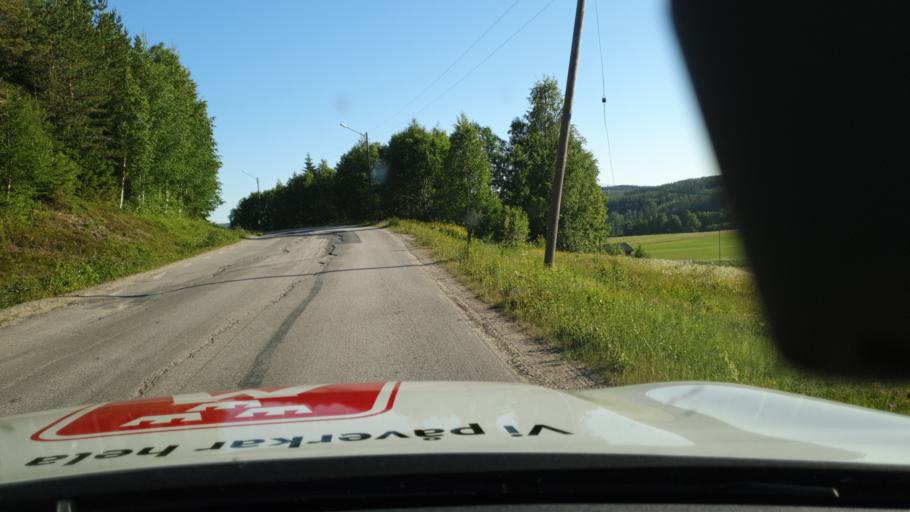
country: SE
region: Vaesterbotten
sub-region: Umea Kommun
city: Roback
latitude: 64.0313
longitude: 20.0842
